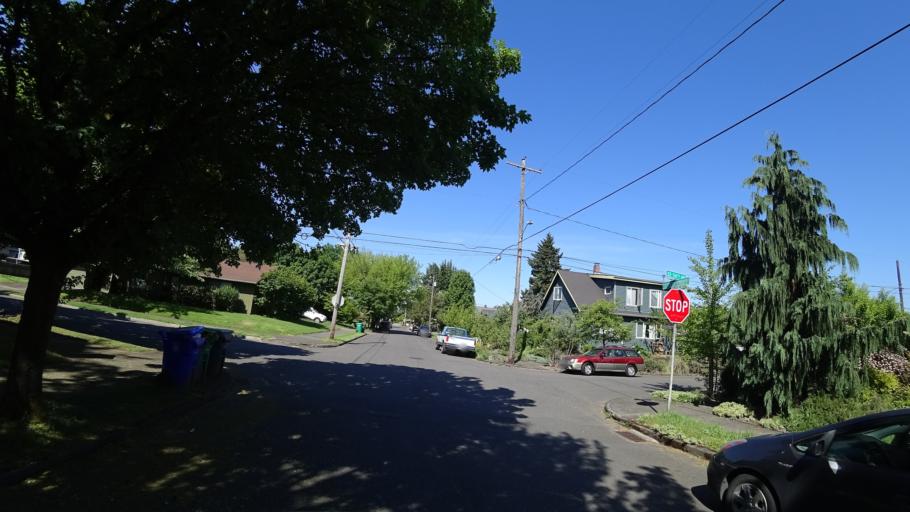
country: US
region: Oregon
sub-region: Multnomah County
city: Lents
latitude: 45.4931
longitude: -122.6070
